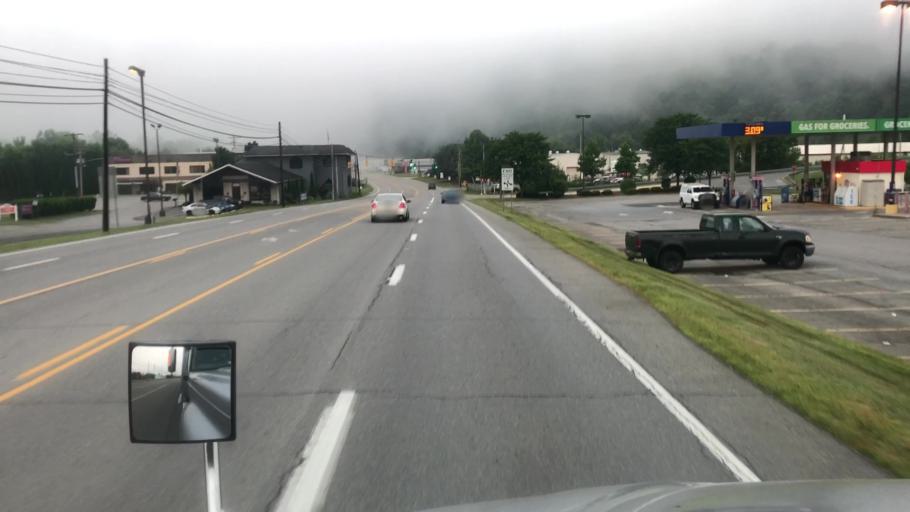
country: US
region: Pennsylvania
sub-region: Venango County
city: Franklin
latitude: 41.4021
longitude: -79.8091
